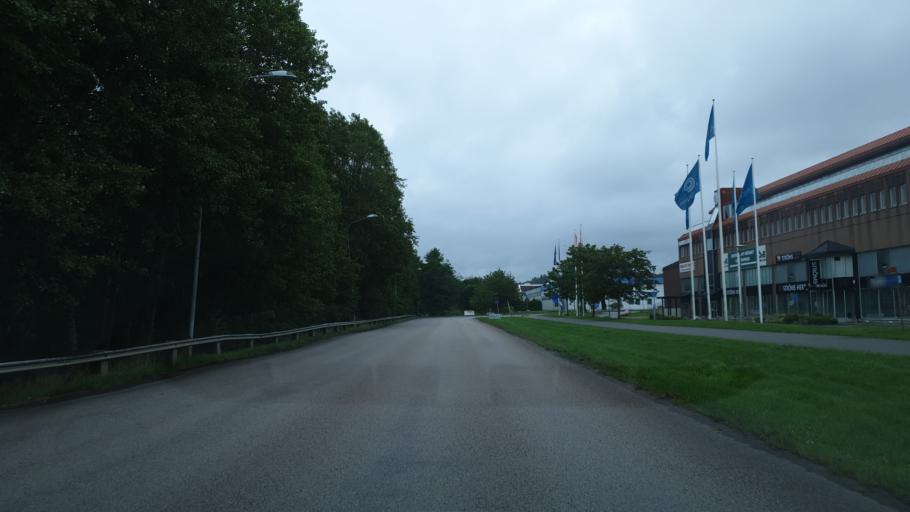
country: SE
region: Vaestra Goetaland
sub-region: Molndal
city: Moelndal
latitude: 57.6414
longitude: 11.9572
